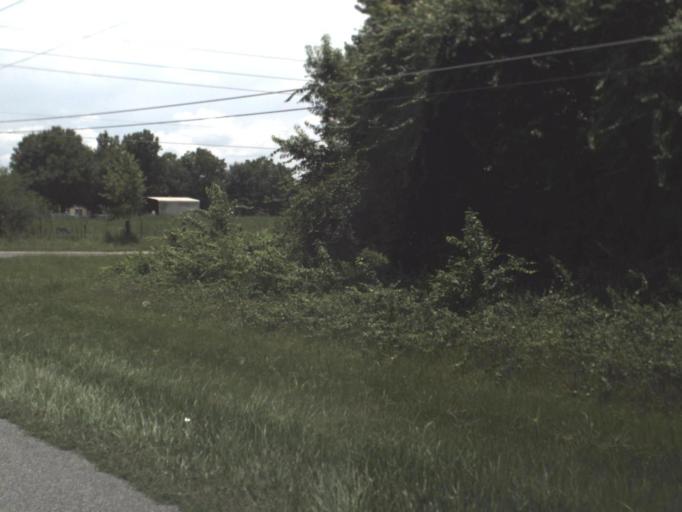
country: US
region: Florida
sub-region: Bradford County
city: Starke
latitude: 29.9977
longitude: -82.1330
